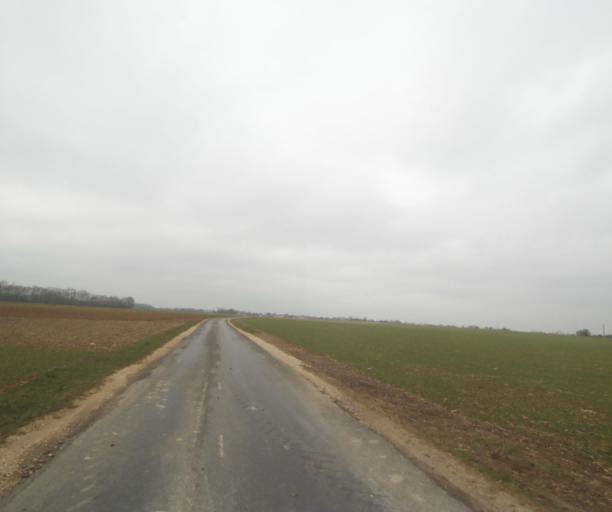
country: FR
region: Champagne-Ardenne
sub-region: Departement de la Haute-Marne
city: Villiers-en-Lieu
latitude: 48.6864
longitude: 4.8202
